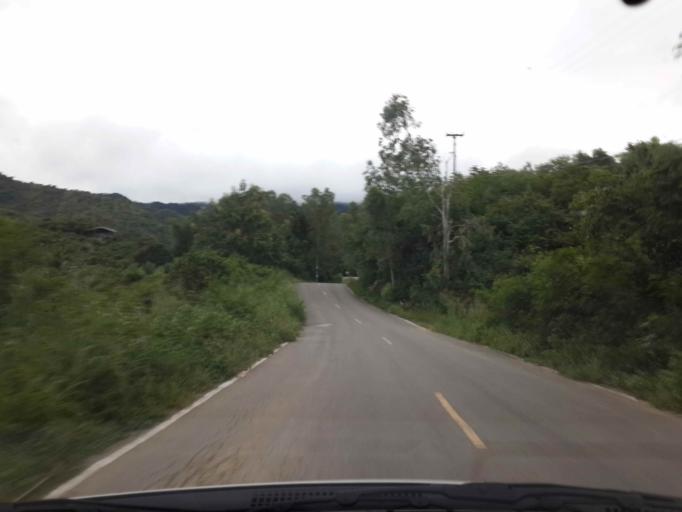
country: TH
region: Ratchaburi
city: Suan Phueng
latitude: 13.5866
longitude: 99.2213
